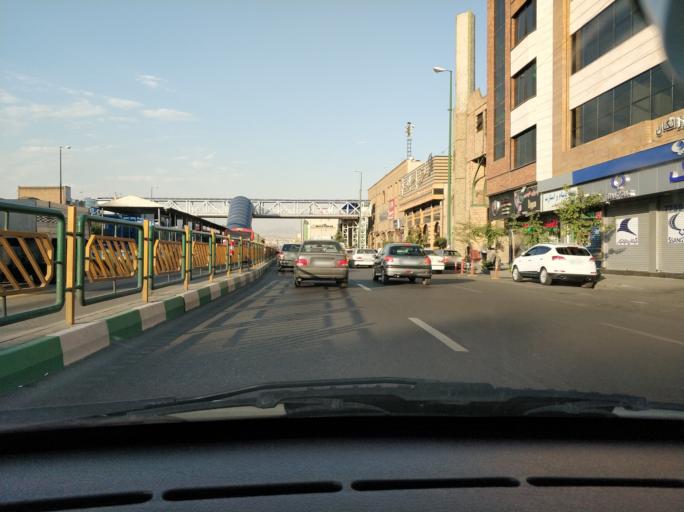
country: IR
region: Tehran
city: Tehran
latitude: 35.7070
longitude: 51.4660
